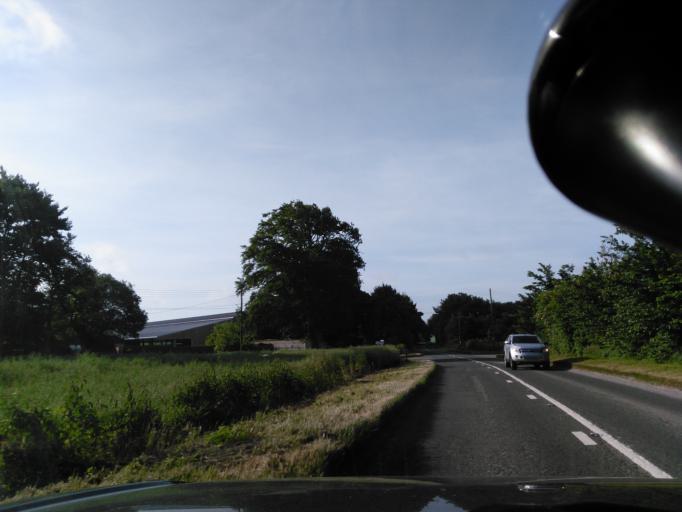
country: GB
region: England
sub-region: Wiltshire
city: Market Lavington
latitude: 51.2586
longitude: -1.9886
